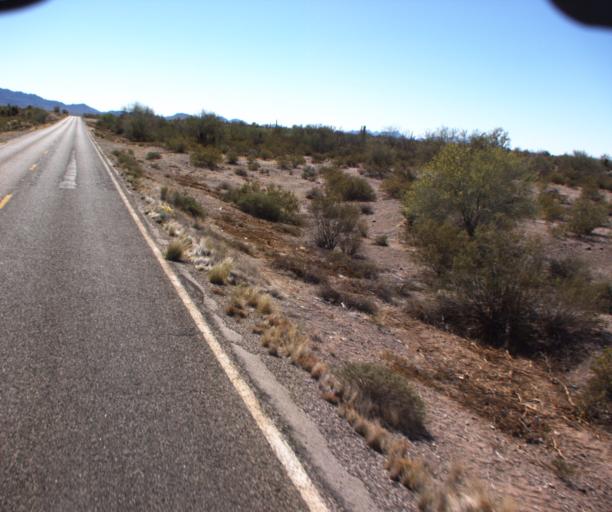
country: US
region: Arizona
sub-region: Pima County
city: Ajo
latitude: 32.3548
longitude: -112.8249
